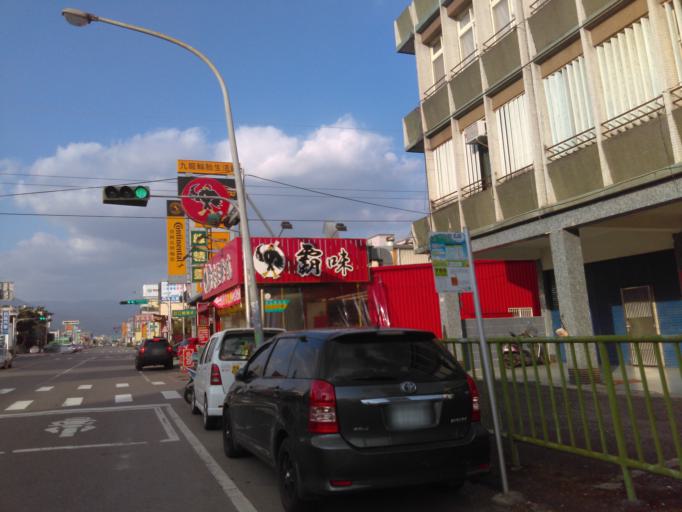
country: TW
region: Taiwan
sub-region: Yilan
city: Yilan
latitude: 24.7715
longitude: 121.7573
